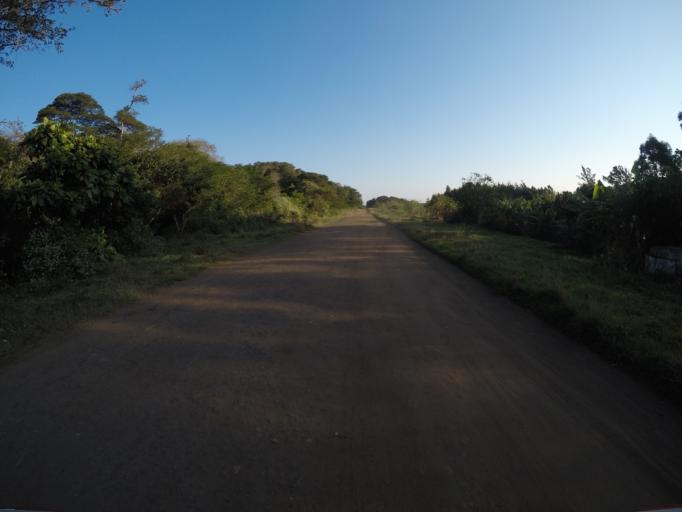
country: ZA
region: KwaZulu-Natal
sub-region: uThungulu District Municipality
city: KwaMbonambi
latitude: -28.6997
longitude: 32.1930
